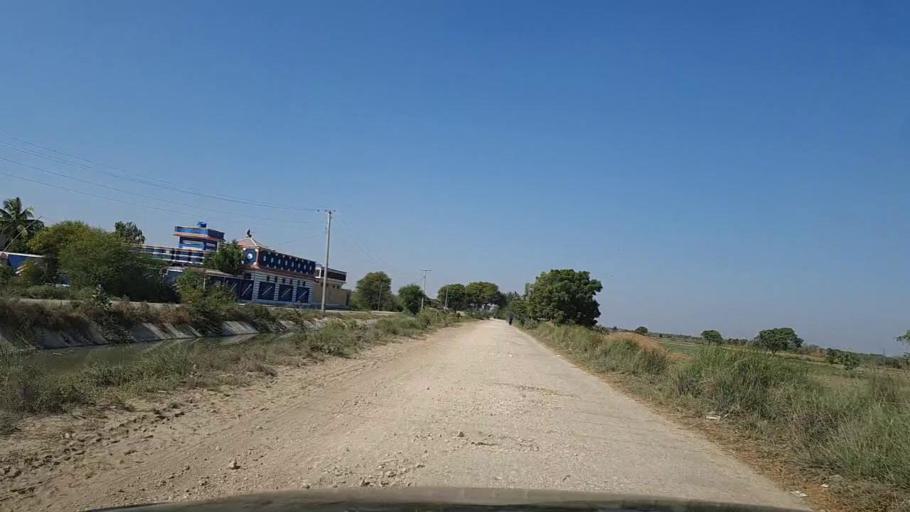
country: PK
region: Sindh
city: Mirpur Sakro
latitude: 24.6119
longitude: 67.7702
